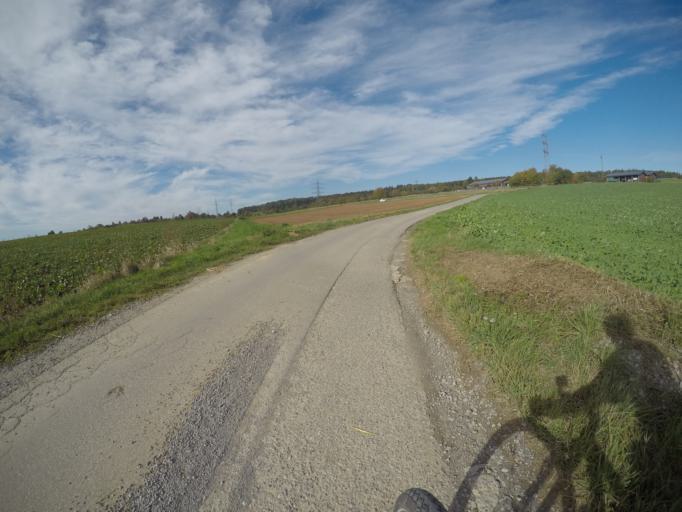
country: DE
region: Baden-Wuerttemberg
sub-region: Regierungsbezirk Stuttgart
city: Gartringen
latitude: 48.6566
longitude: 8.9150
